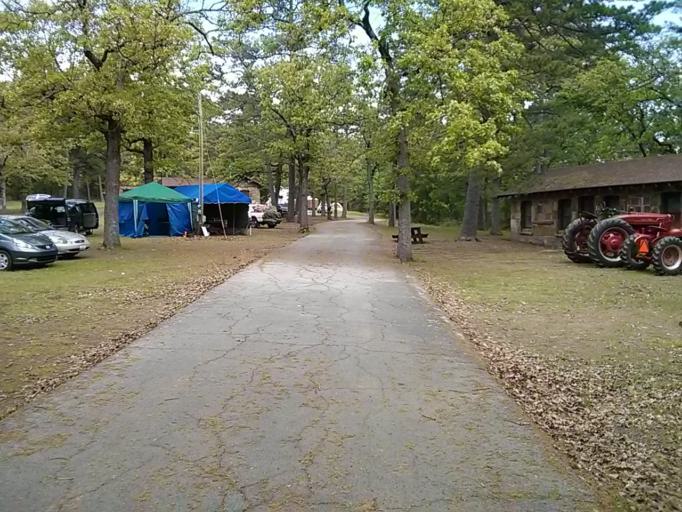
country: US
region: Oklahoma
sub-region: Latimer County
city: Wilburton
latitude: 35.0046
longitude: -95.3362
